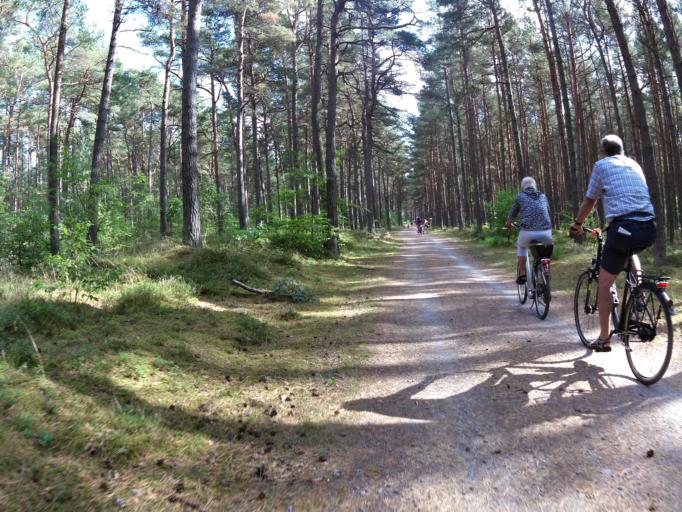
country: DE
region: Mecklenburg-Vorpommern
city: Karlshagen
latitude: 54.1049
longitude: 13.8544
